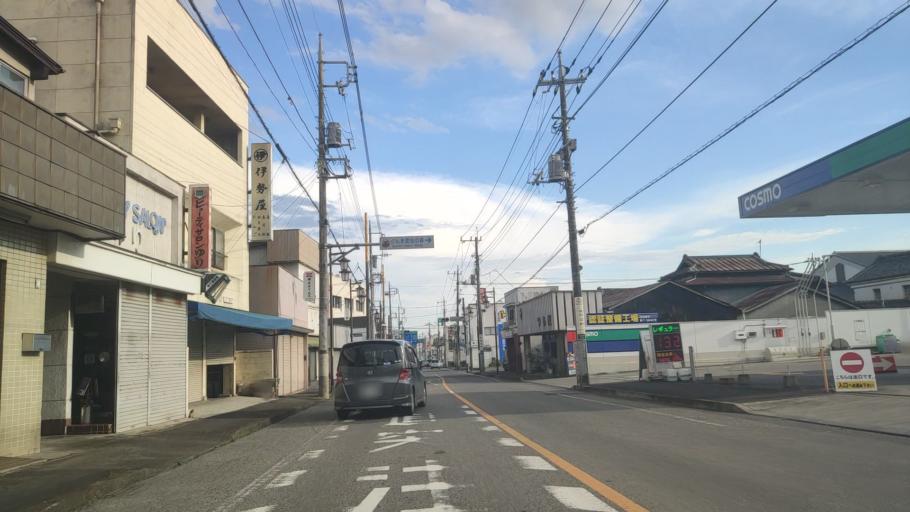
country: JP
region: Gunma
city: Omamacho-omama
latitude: 36.4310
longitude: 139.2751
